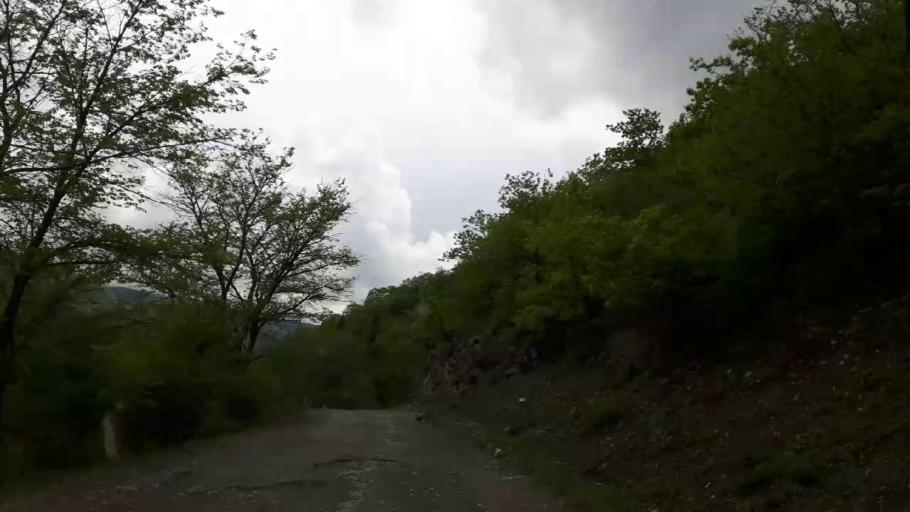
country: GE
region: Shida Kartli
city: Gori
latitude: 41.8781
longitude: 43.9905
